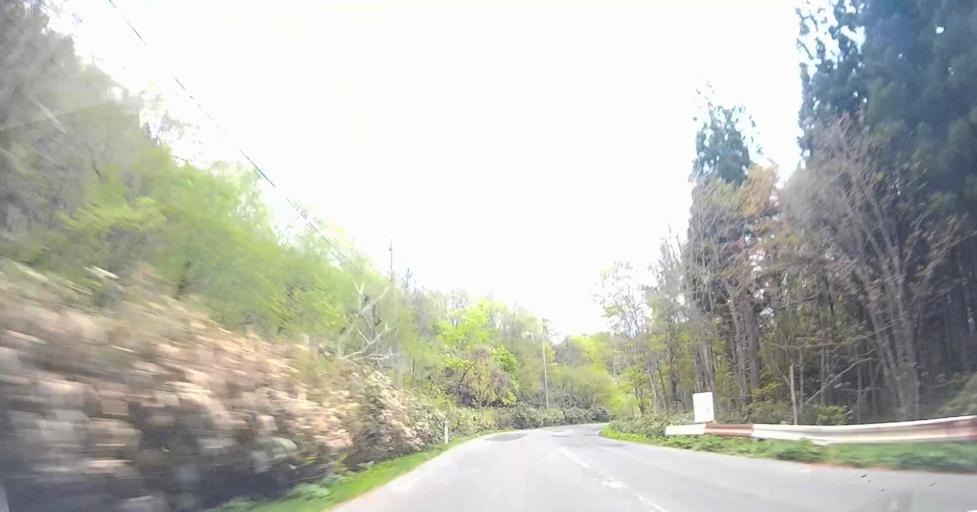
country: JP
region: Aomori
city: Goshogawara
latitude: 41.1156
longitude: 140.5282
